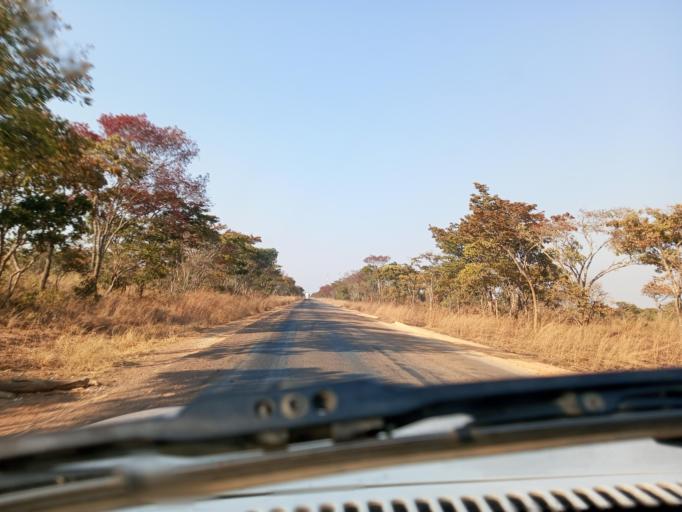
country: ZM
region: Northern
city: Mpika
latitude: -12.4072
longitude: 31.0857
